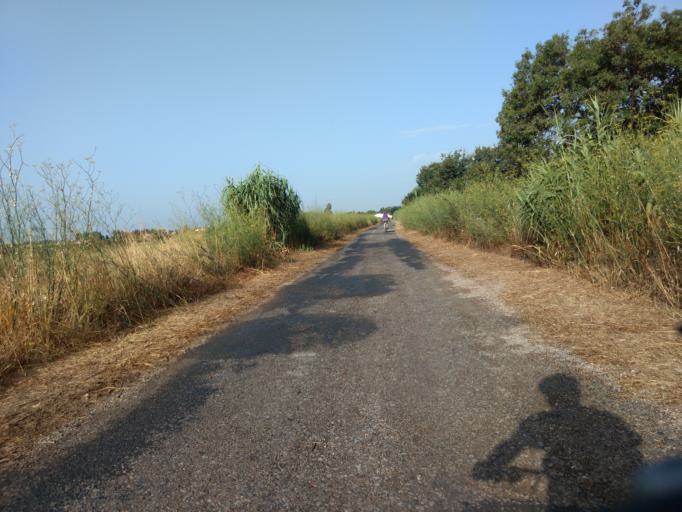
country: FR
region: Languedoc-Roussillon
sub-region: Departement des Pyrenees-Orientales
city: Saint-Laurent-de-la-Salanque
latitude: 42.7653
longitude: 2.9972
